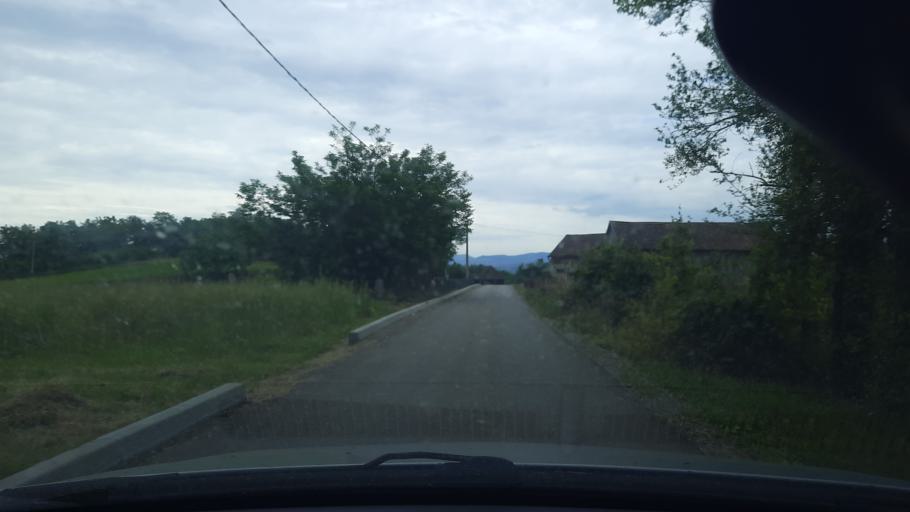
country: RS
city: Jarebice
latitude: 44.4996
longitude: 19.4760
